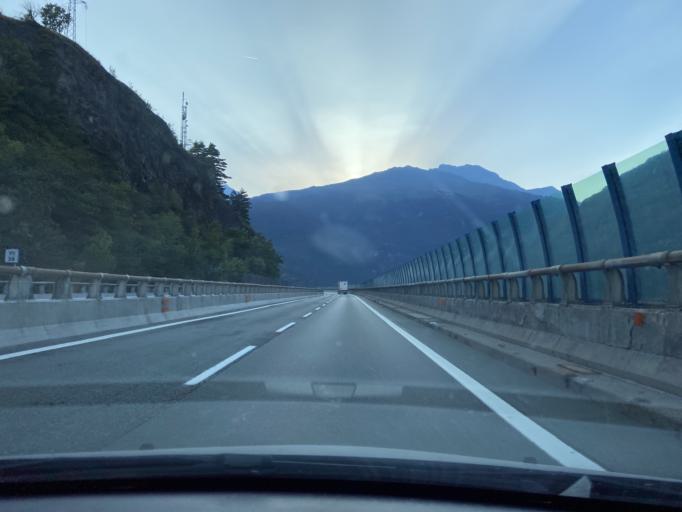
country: IT
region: Piedmont
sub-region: Provincia di Torino
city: San Giuseppe
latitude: 45.1444
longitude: 7.0469
